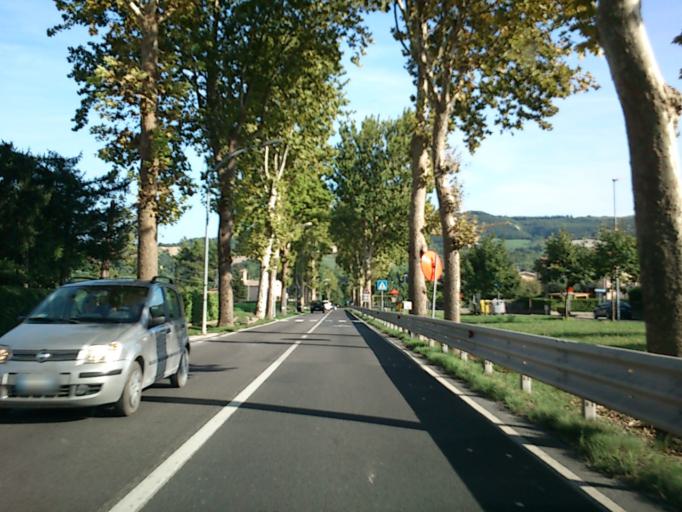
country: IT
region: The Marches
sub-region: Provincia di Pesaro e Urbino
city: Fermignano
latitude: 43.6975
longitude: 12.6658
